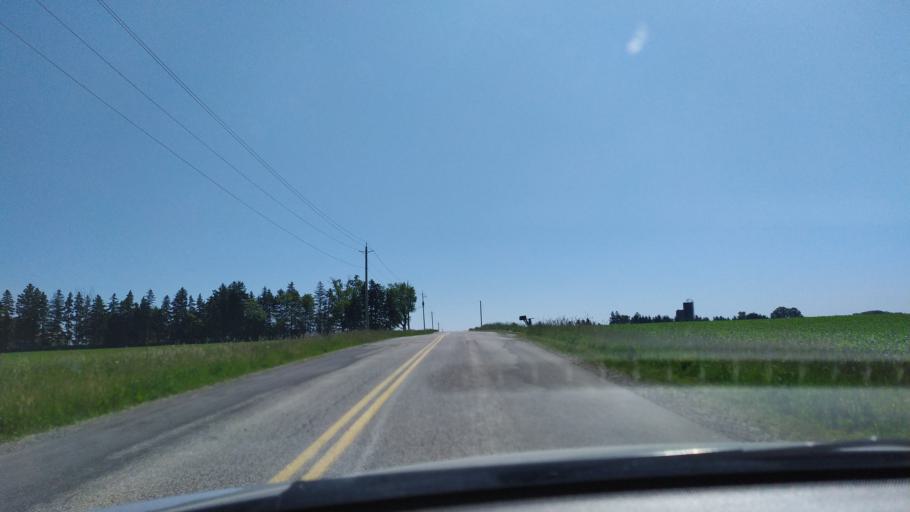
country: CA
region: Ontario
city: Stratford
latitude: 43.4547
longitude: -80.7469
